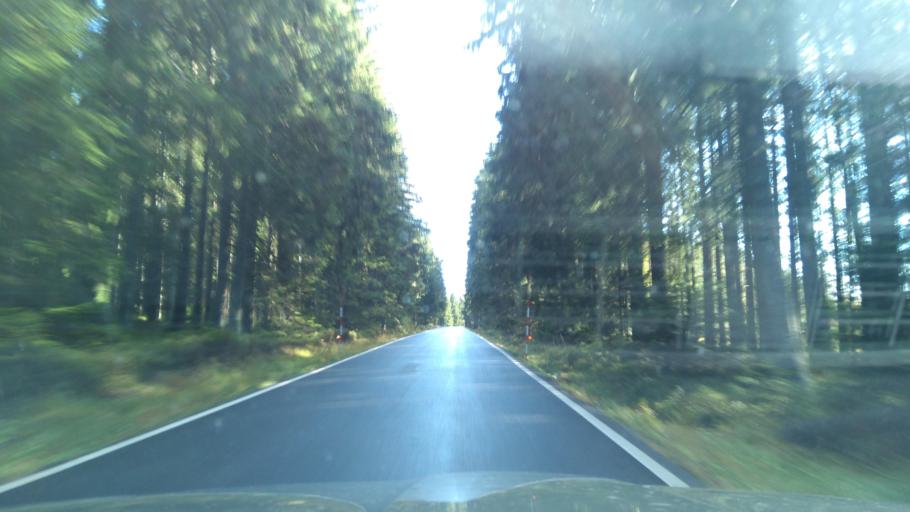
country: CZ
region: Plzensky
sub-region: Okres Klatovy
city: Kasperske Hory
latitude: 49.0278
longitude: 13.5462
